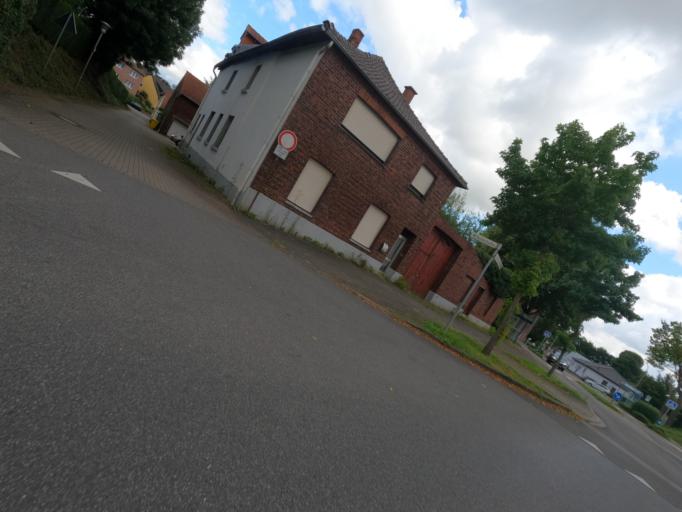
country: DE
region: North Rhine-Westphalia
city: Baesweiler
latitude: 50.9378
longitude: 6.2052
